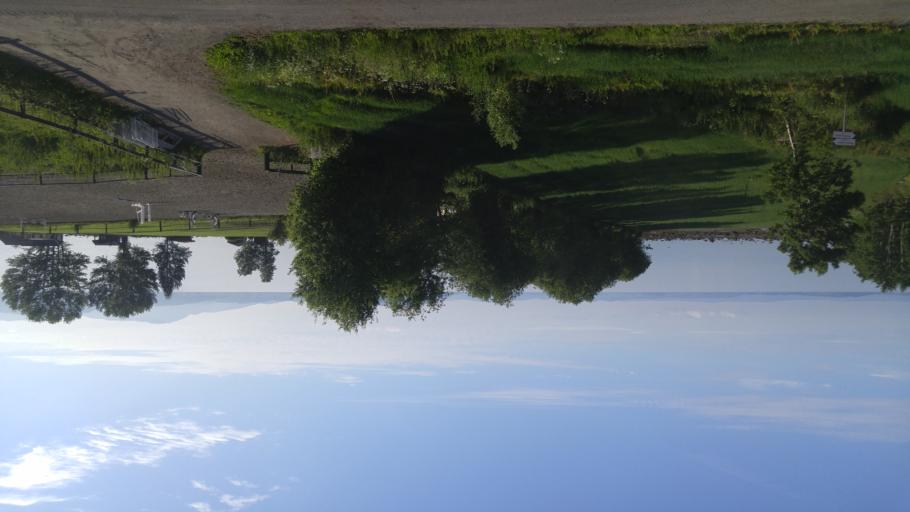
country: NO
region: Sor-Trondelag
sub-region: Malvik
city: Malvik
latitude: 63.4364
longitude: 10.6824
